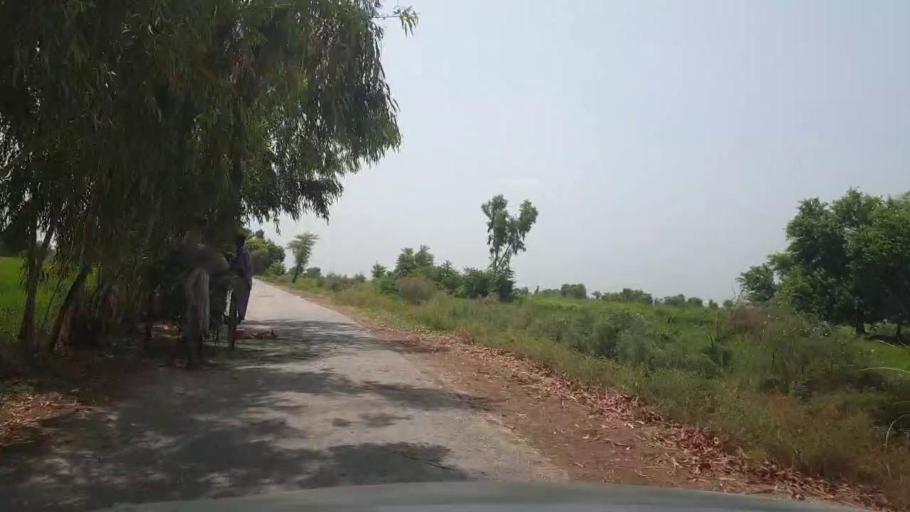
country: PK
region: Sindh
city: Garhi Yasin
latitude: 27.9441
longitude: 68.3756
